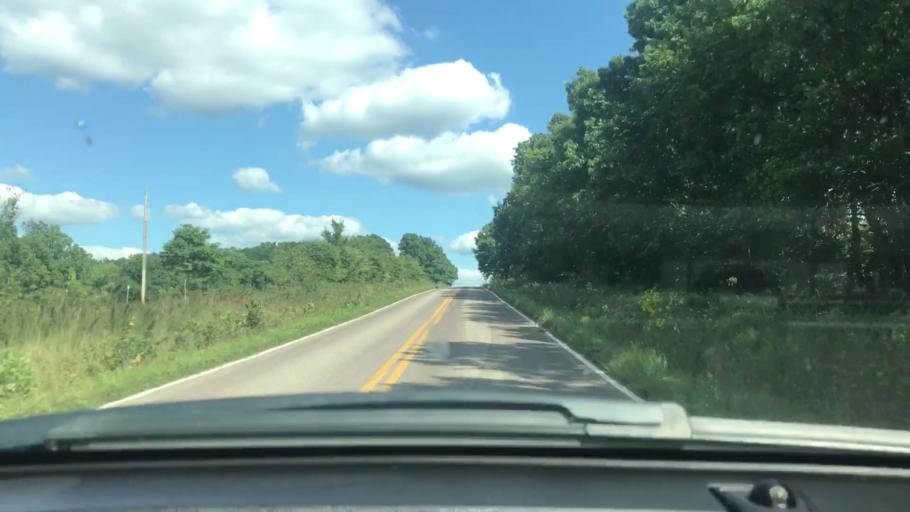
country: US
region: Missouri
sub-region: Wright County
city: Hartville
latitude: 37.3766
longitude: -92.3781
